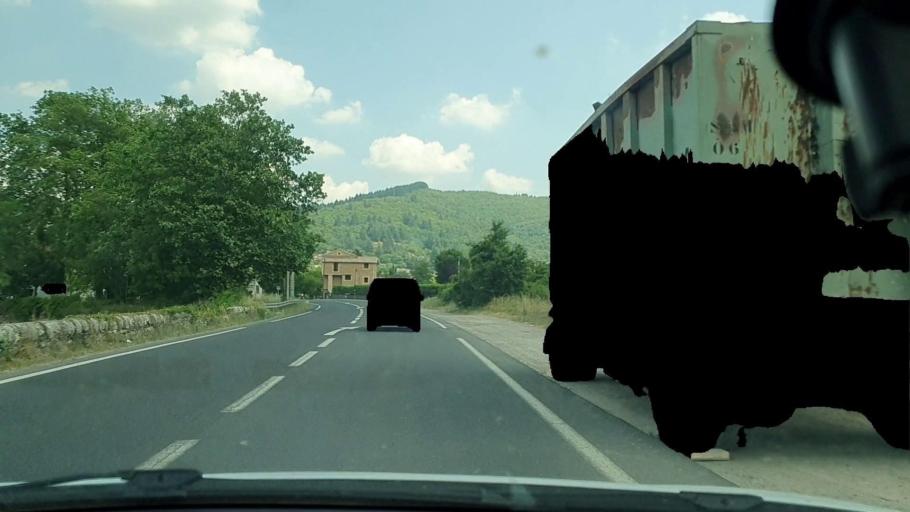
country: FR
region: Languedoc-Roussillon
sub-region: Departement du Gard
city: Aveze
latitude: 43.9735
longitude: 3.5904
